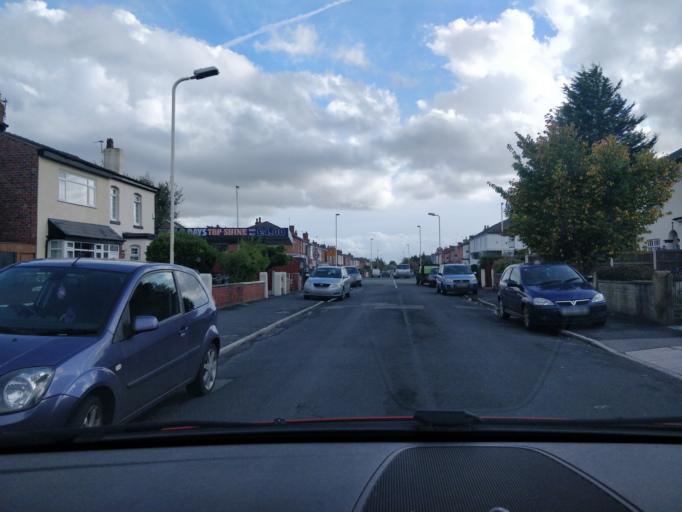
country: GB
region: England
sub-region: Sefton
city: Southport
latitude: 53.6315
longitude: -3.0090
